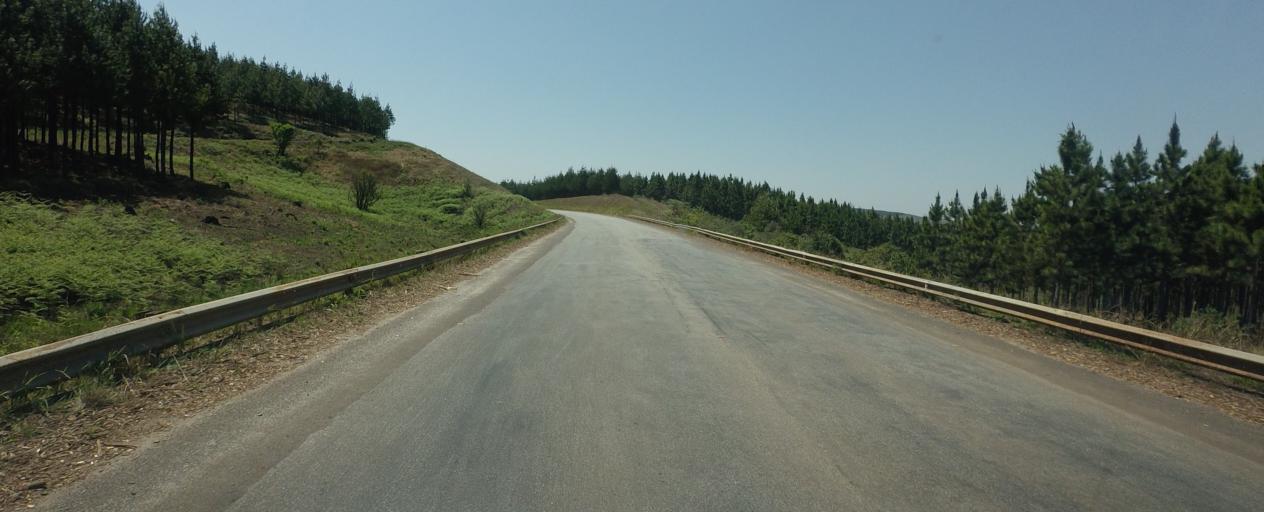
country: ZA
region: Mpumalanga
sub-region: Ehlanzeni District
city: Graksop
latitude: -24.9089
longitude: 30.8435
